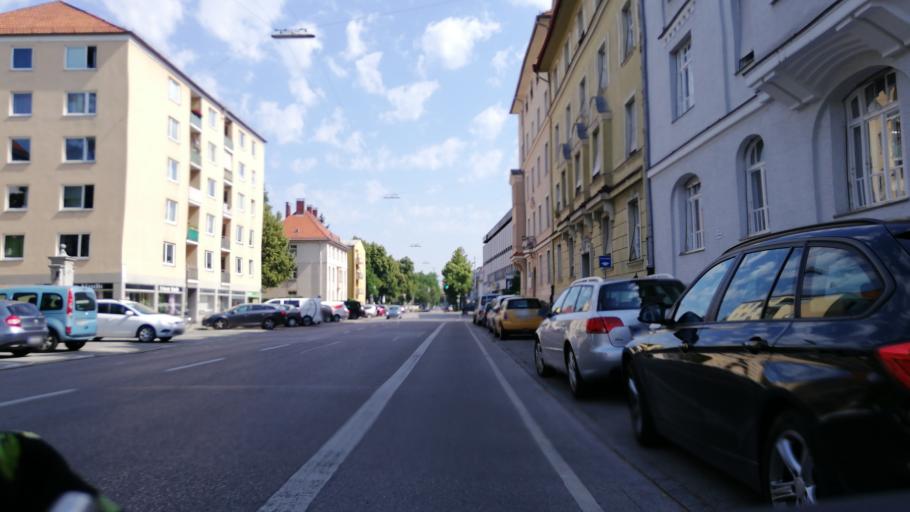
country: DE
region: Bavaria
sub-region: Upper Bavaria
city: Munich
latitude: 48.1586
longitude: 11.5610
